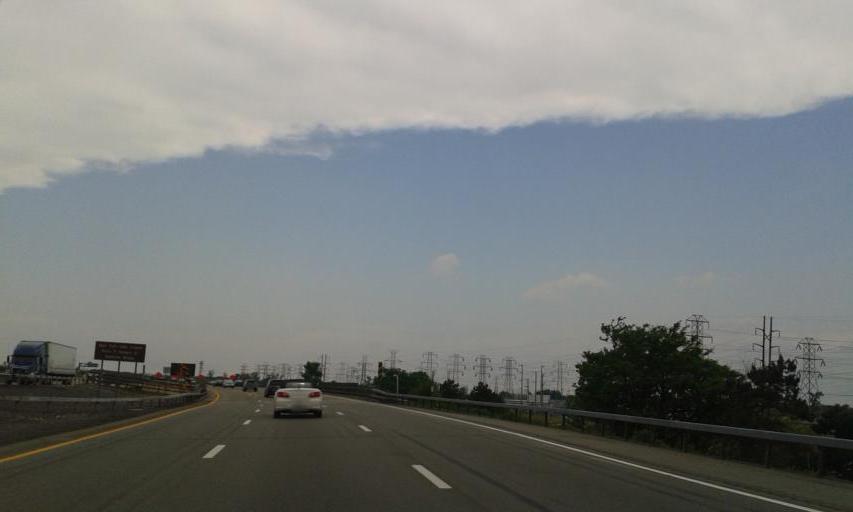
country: US
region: New York
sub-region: Erie County
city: Tonawanda
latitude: 43.0005
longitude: -78.8518
